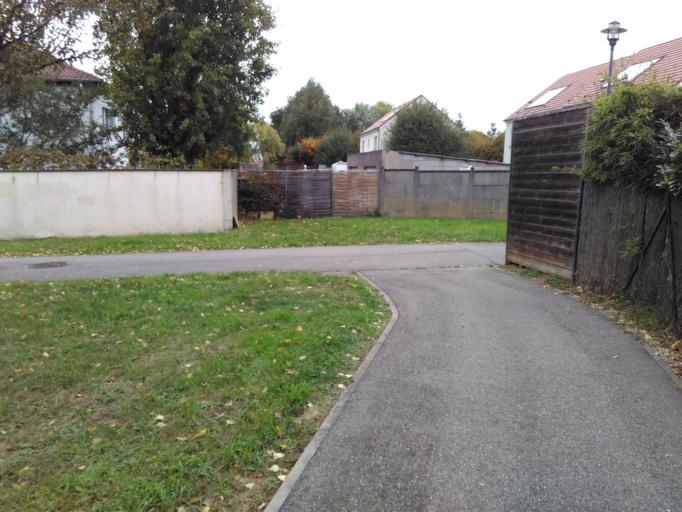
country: FR
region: Lorraine
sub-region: Departement de Meurthe-et-Moselle
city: Essey-les-Nancy
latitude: 48.7030
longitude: 6.2256
